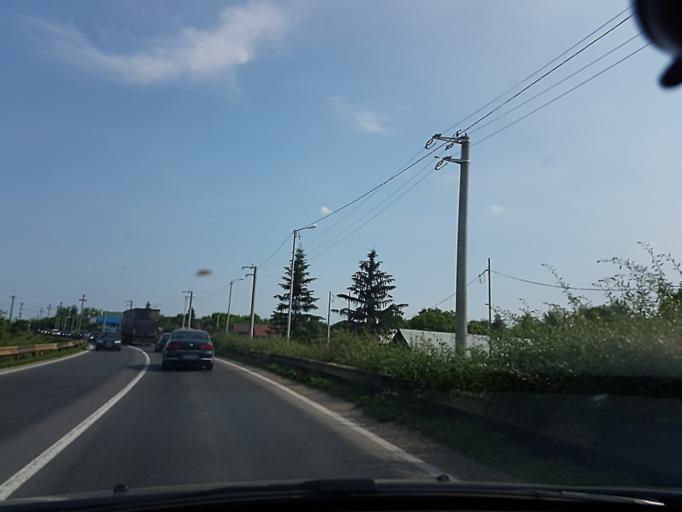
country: RO
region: Prahova
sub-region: Comuna Blejoiu
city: Blejoi
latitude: 44.9931
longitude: 26.0127
